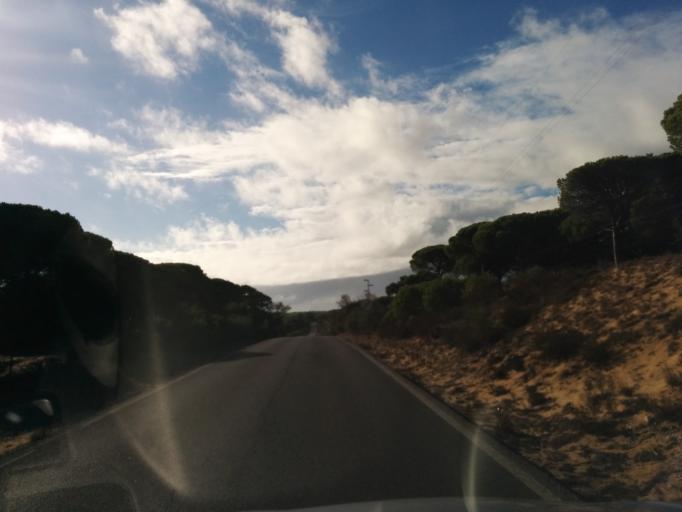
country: ES
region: Andalusia
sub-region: Provincia de Cadiz
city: Vejer de la Frontera
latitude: 36.1920
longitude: -5.9836
